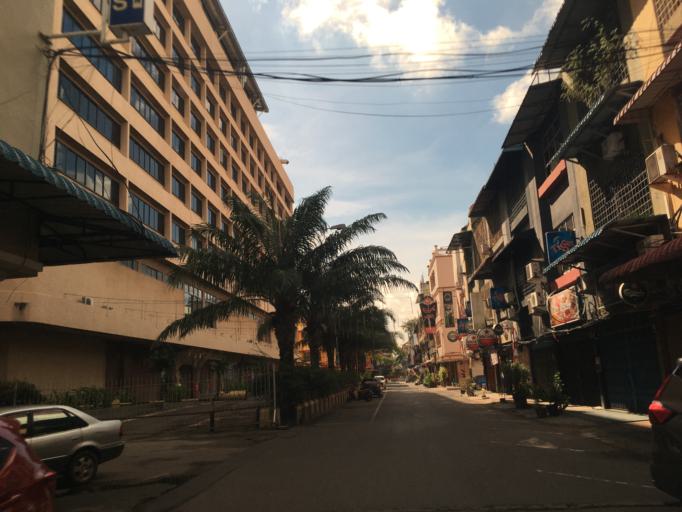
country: SG
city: Singapore
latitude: 1.1495
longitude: 104.0072
